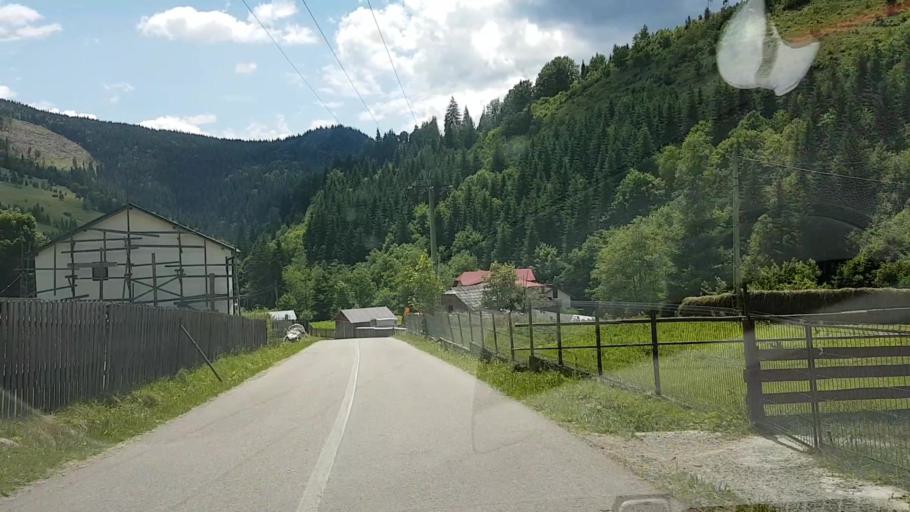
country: RO
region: Suceava
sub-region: Comuna Crucea
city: Crucea
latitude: 47.4215
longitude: 25.5792
